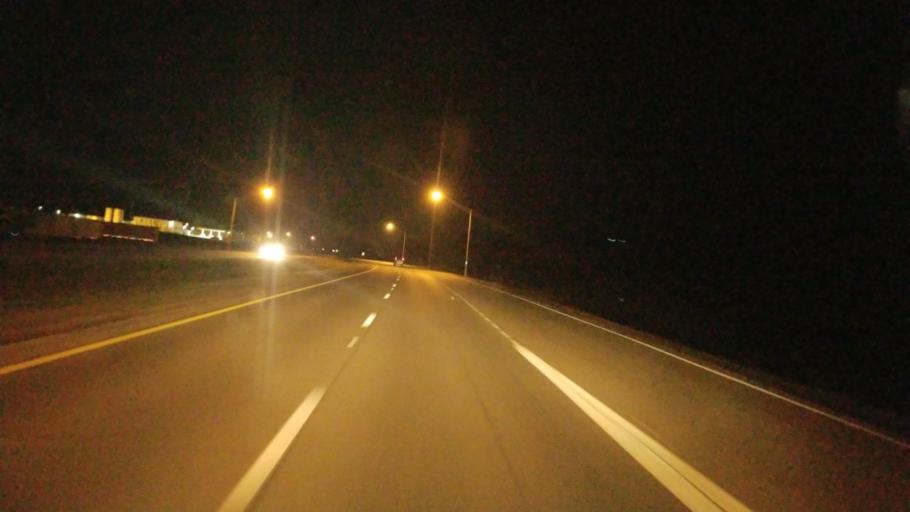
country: US
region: Ohio
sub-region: Pike County
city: Piketon
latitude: 39.0161
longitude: -83.0255
